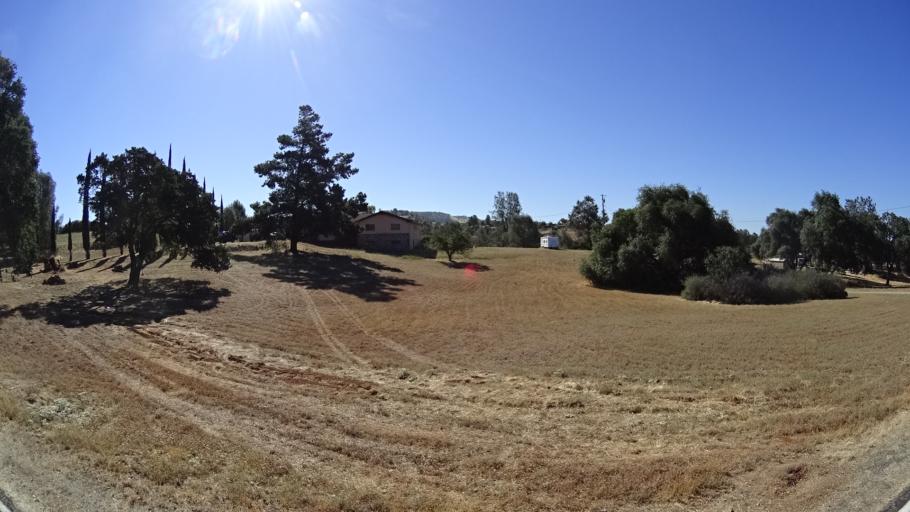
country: US
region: California
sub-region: Calaveras County
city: Rancho Calaveras
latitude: 38.1265
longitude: -120.8561
